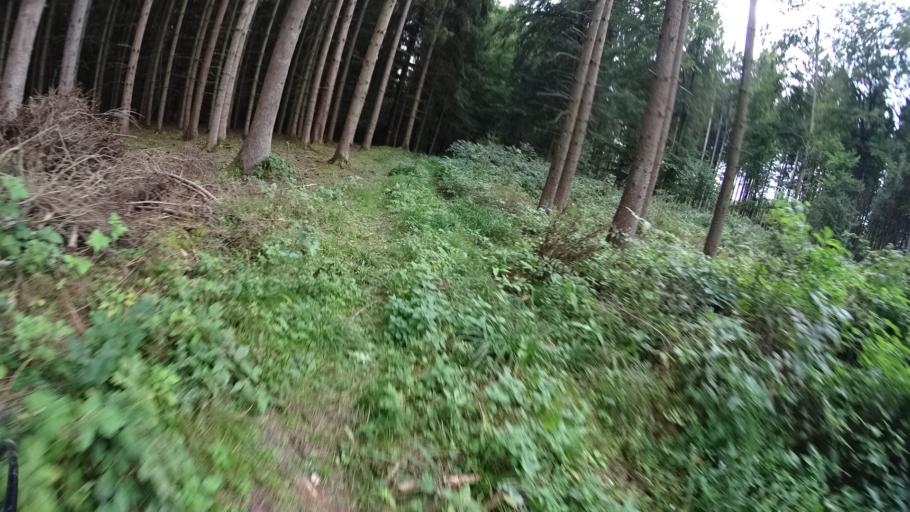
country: DE
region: Bavaria
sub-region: Upper Bavaria
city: Bohmfeld
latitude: 48.8821
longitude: 11.3378
